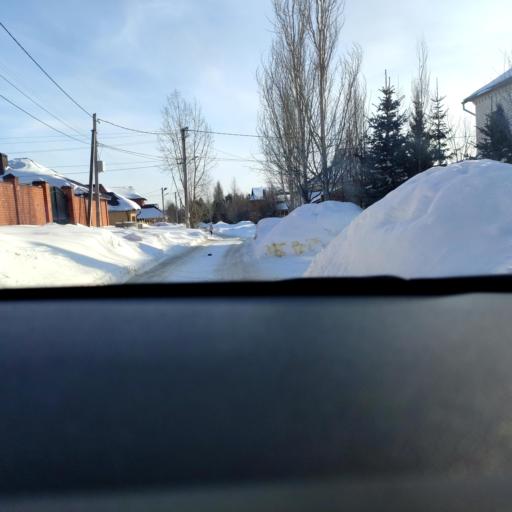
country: RU
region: Tatarstan
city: Vysokaya Gora
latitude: 55.8084
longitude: 49.2456
